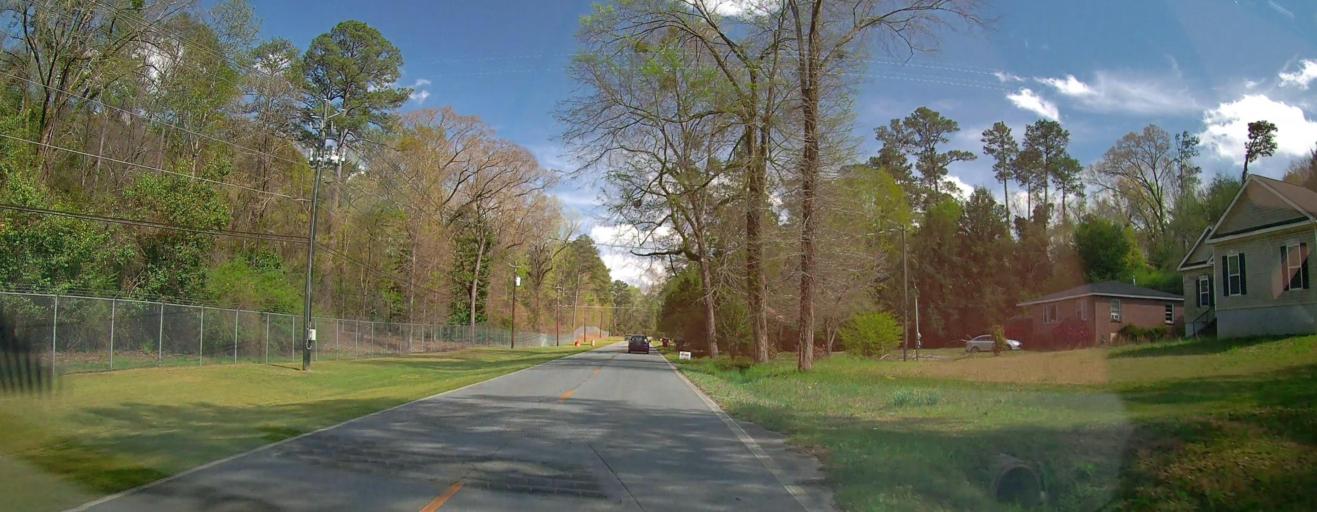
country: US
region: Georgia
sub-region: Bibb County
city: Macon
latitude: 32.8159
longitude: -83.5456
